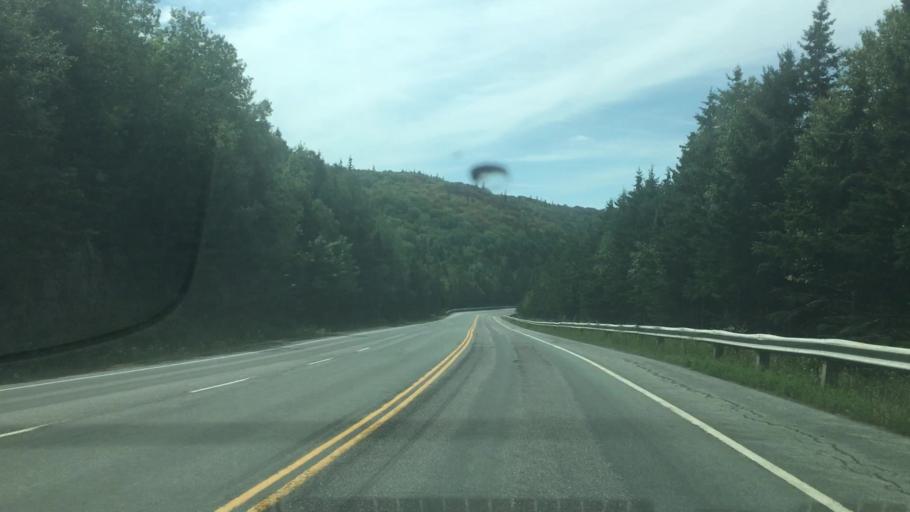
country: CA
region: Nova Scotia
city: Sydney Mines
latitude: 46.2428
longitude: -60.5597
